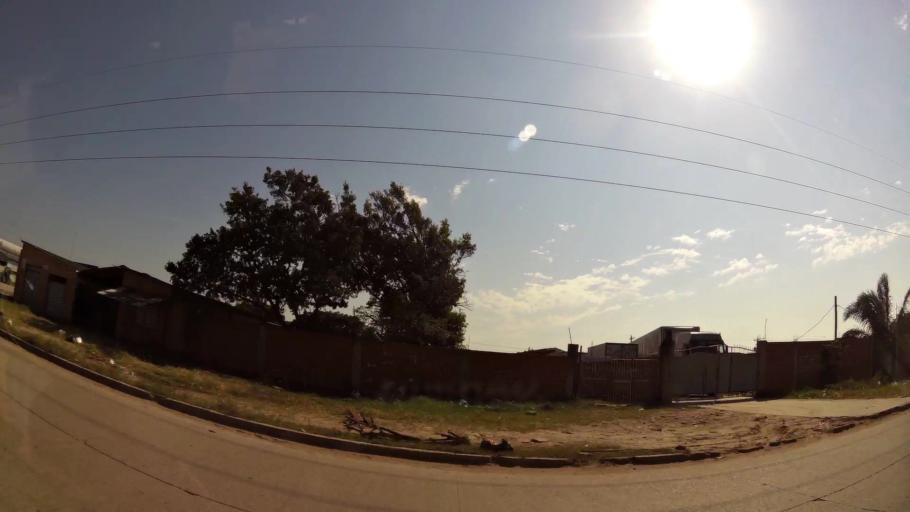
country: BO
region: Santa Cruz
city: Cotoca
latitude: -17.7857
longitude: -63.1081
